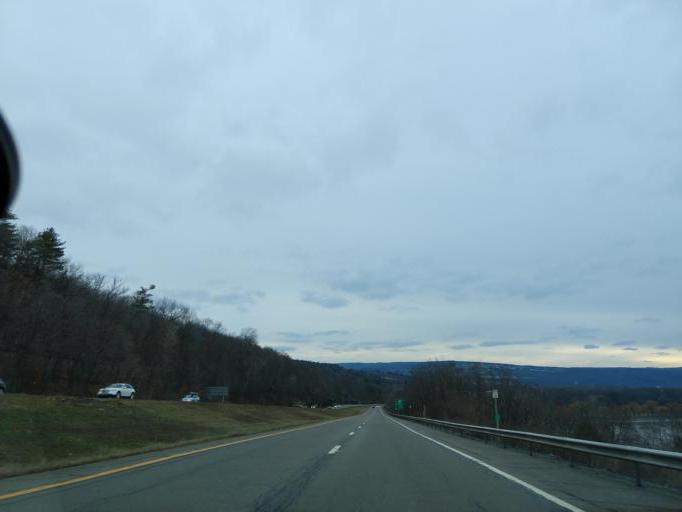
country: US
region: New York
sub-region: Tompkins County
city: Cayuga Heights
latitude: 42.4709
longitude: -76.5006
